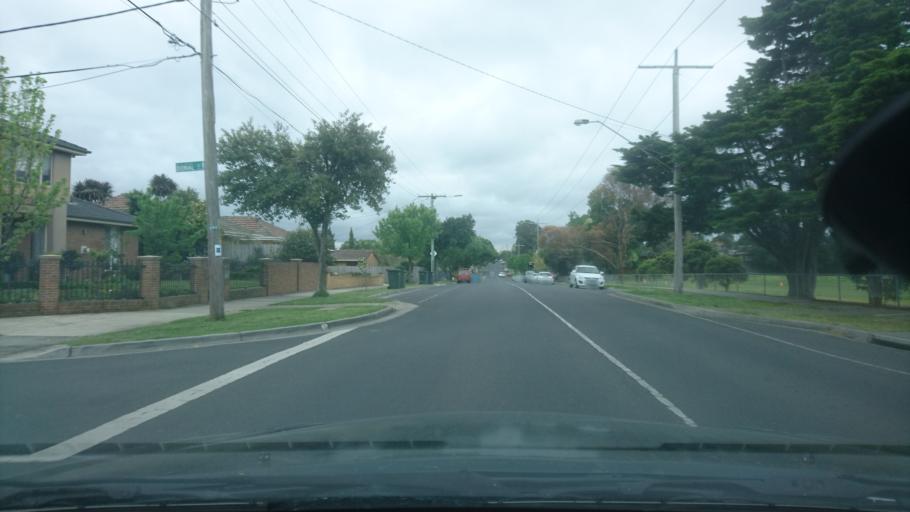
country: AU
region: Victoria
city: Murrumbeena
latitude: -37.9064
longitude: 145.0746
